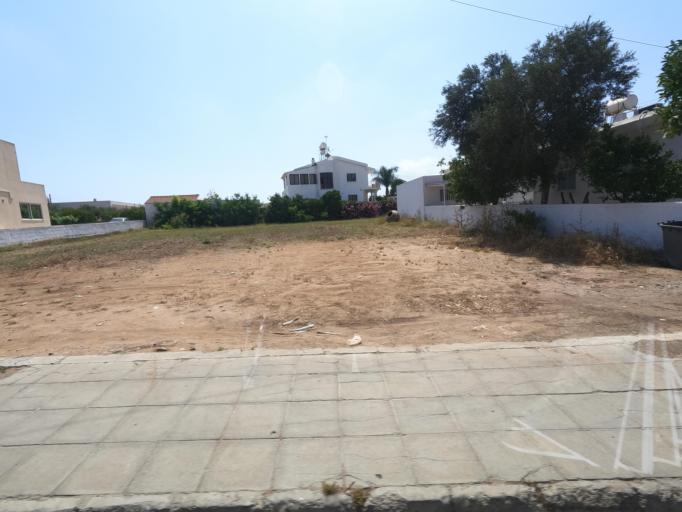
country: CY
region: Ammochostos
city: Paralimni
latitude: 35.0459
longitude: 33.9822
